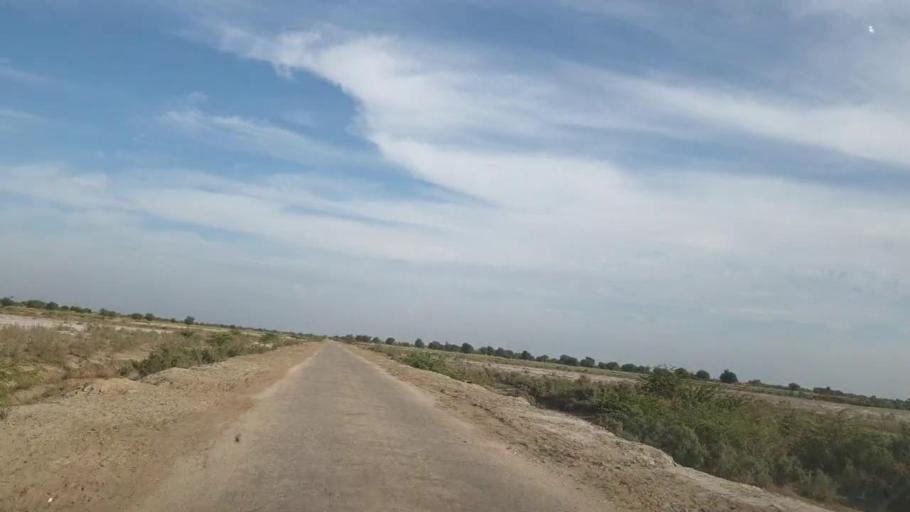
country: PK
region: Sindh
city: Pithoro
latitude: 25.6375
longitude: 69.3863
